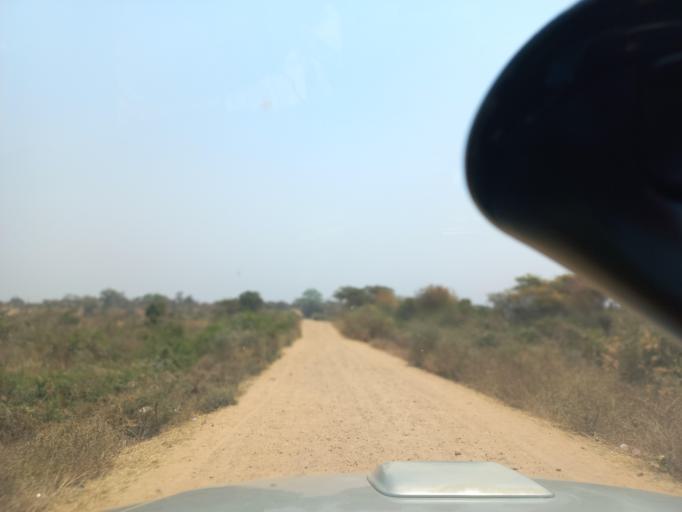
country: ZW
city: Chirundu
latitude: -15.9428
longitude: 28.8448
